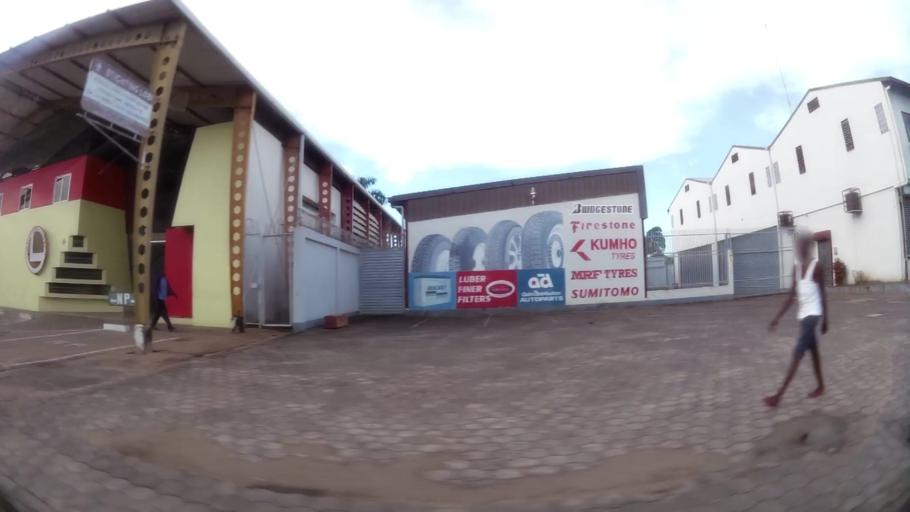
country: SR
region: Paramaribo
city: Paramaribo
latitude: 5.8182
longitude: -55.1787
